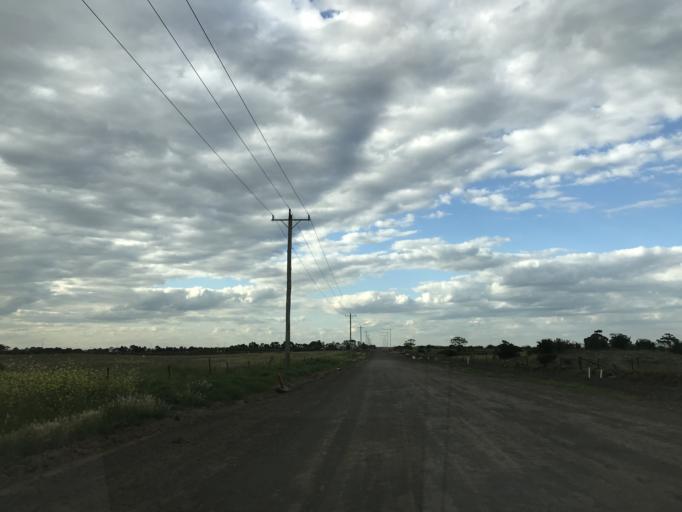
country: AU
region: Victoria
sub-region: Wyndham
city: Truganina
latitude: -37.8178
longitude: 144.7221
